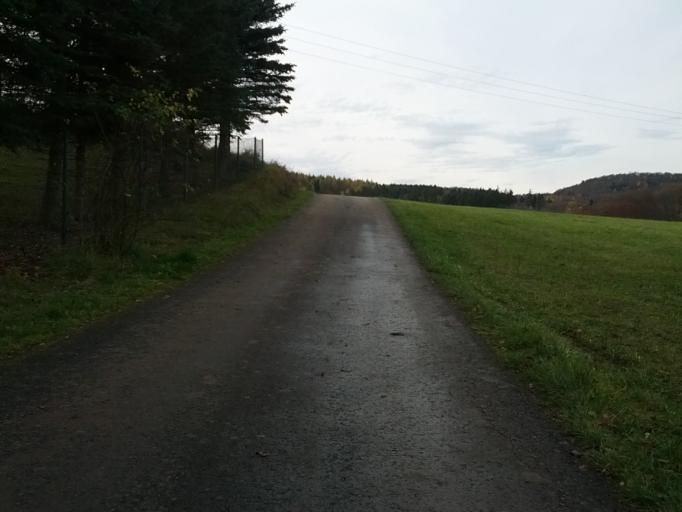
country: DE
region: Thuringia
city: Ruhla
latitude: 50.9334
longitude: 10.3496
